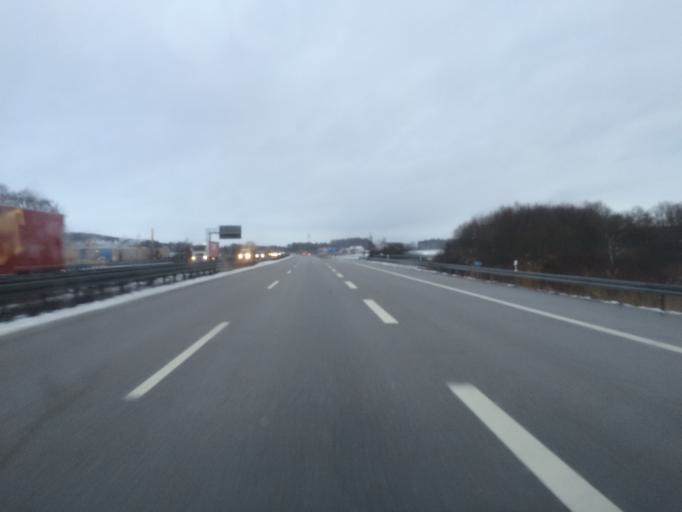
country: DE
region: Bavaria
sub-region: Upper Palatinate
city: Wackersdorf
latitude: 49.3129
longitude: 12.1539
